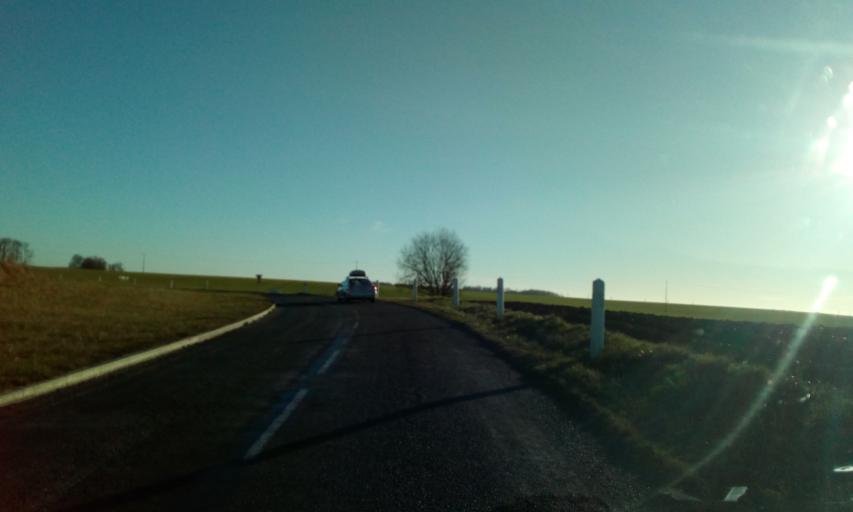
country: FR
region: Picardie
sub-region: Departement de l'Aisne
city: Rozoy-sur-Serre
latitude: 49.6998
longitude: 4.1604
